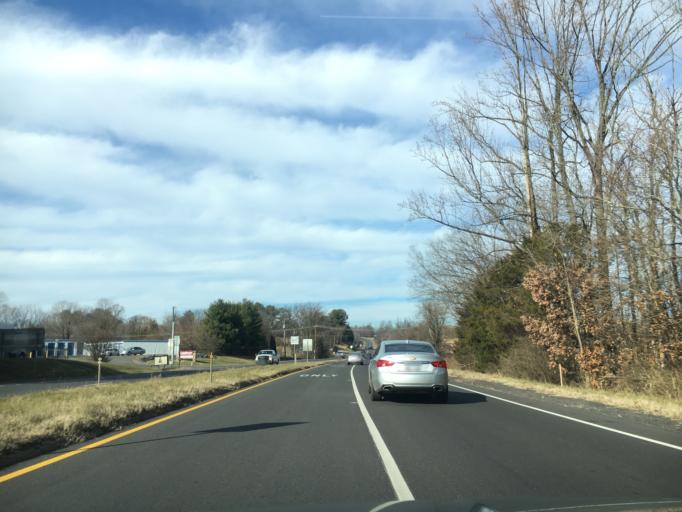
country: US
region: Virginia
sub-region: Culpeper County
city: Culpeper
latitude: 38.4516
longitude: -77.9850
